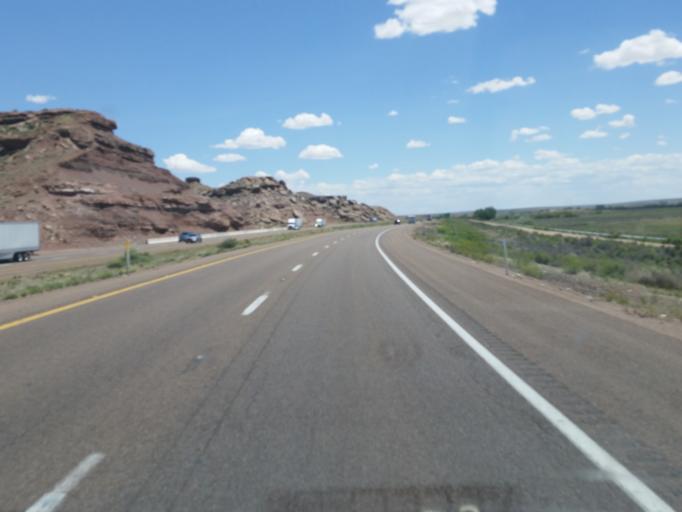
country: US
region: Arizona
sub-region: Navajo County
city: Joseph City
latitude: 34.9389
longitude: -110.2796
